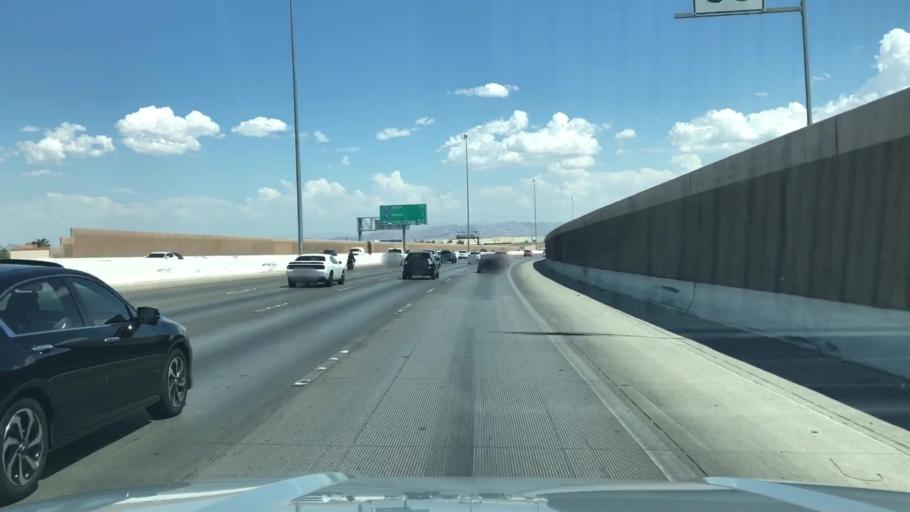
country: US
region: Nevada
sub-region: Clark County
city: Paradise
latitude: 36.0684
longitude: -115.1982
